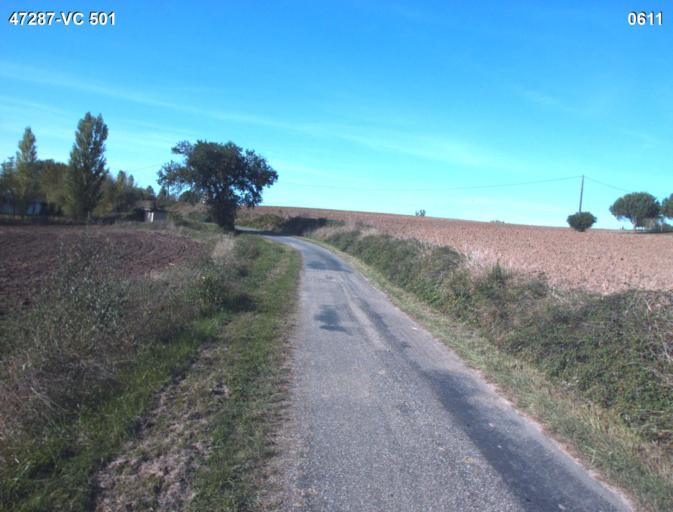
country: FR
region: Aquitaine
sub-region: Departement du Lot-et-Garonne
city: Laplume
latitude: 44.1150
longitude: 0.4599
